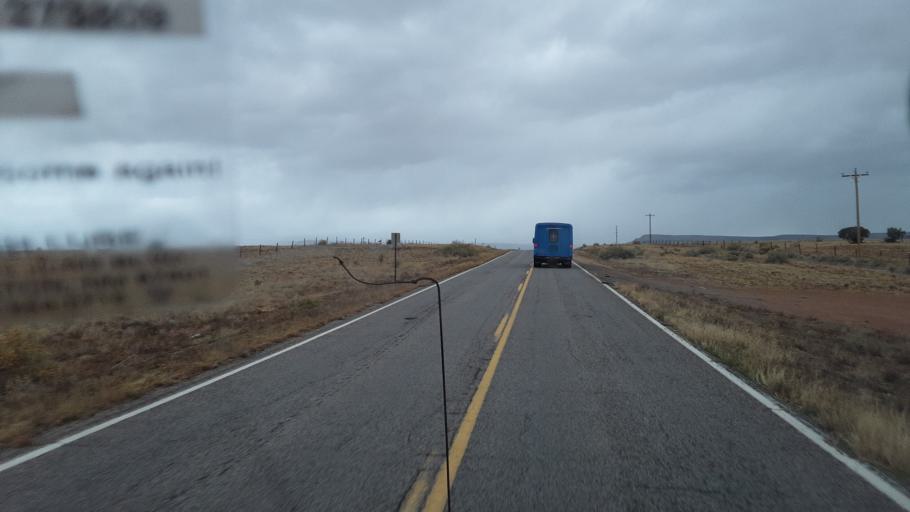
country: US
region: New Mexico
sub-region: Rio Arriba County
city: Santa Teresa
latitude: 36.2627
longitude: -106.4193
